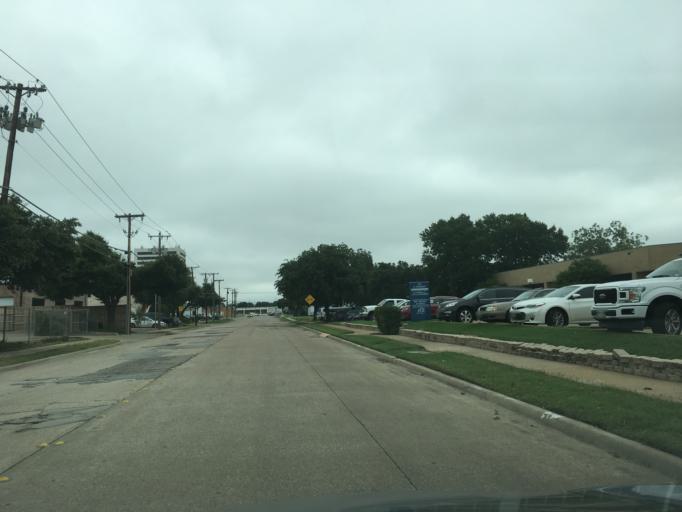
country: US
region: Texas
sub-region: Dallas County
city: Richardson
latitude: 32.9474
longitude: -96.7348
